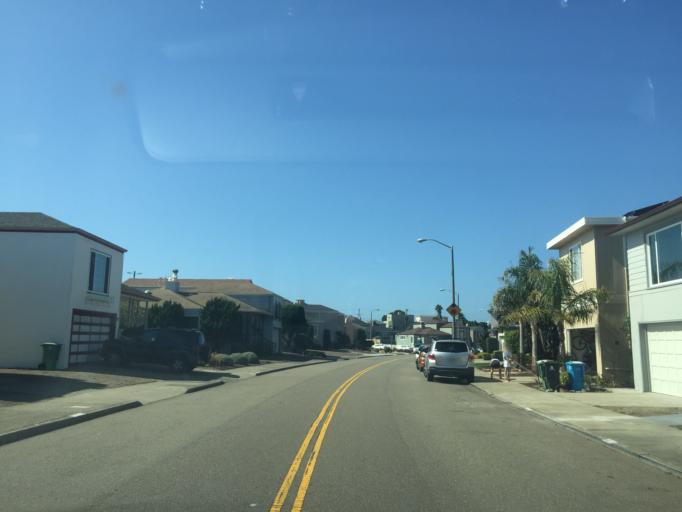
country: US
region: California
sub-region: San Mateo County
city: Daly City
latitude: 37.7352
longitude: -122.4890
